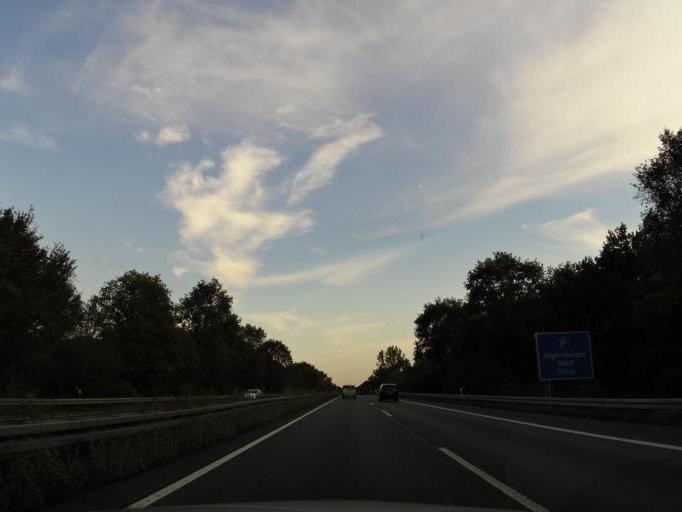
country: DE
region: Hesse
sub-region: Regierungsbezirk Darmstadt
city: Einhausen
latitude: 49.7042
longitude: 8.5476
